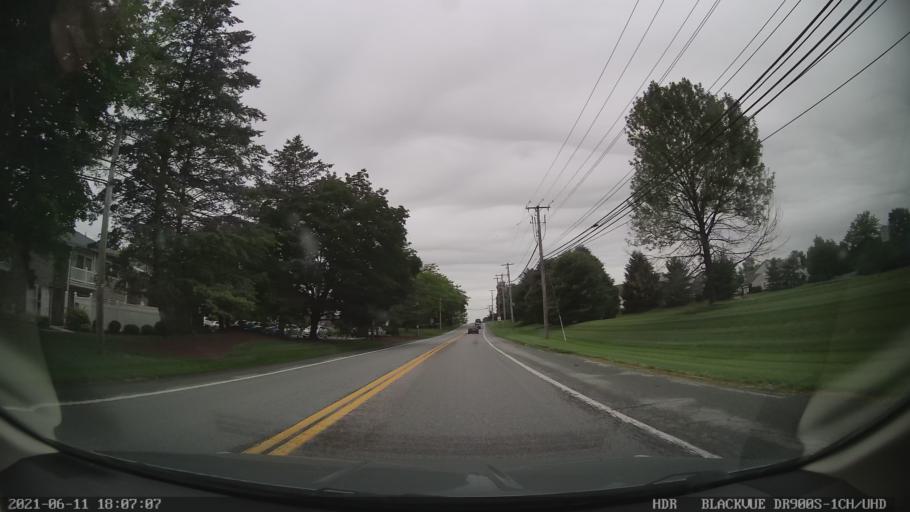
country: US
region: Pennsylvania
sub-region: Berks County
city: Spring Ridge
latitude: 40.3426
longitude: -75.9940
